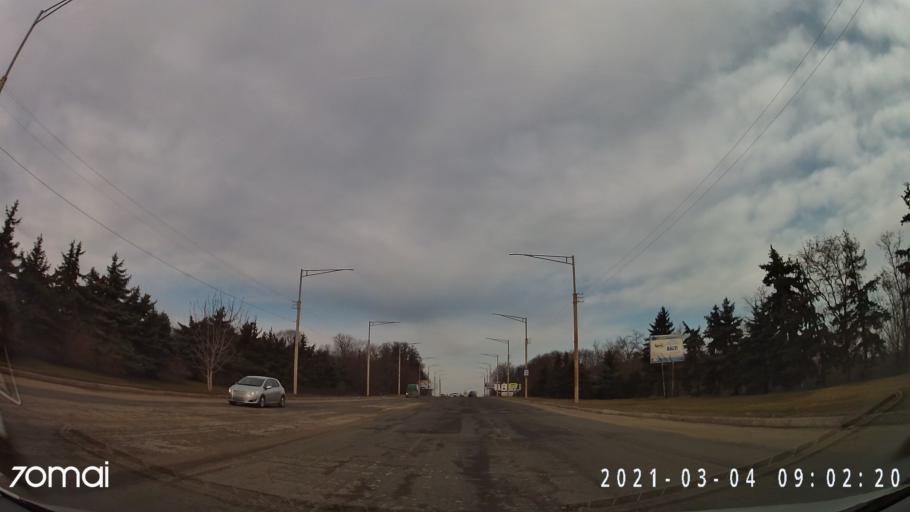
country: MD
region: Balti
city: Balti
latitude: 47.7422
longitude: 27.9561
